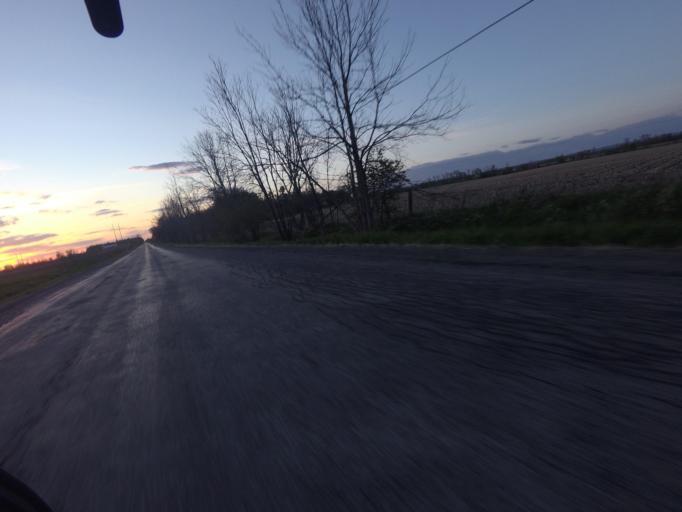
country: CA
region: Ontario
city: Arnprior
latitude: 45.4105
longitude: -76.2133
